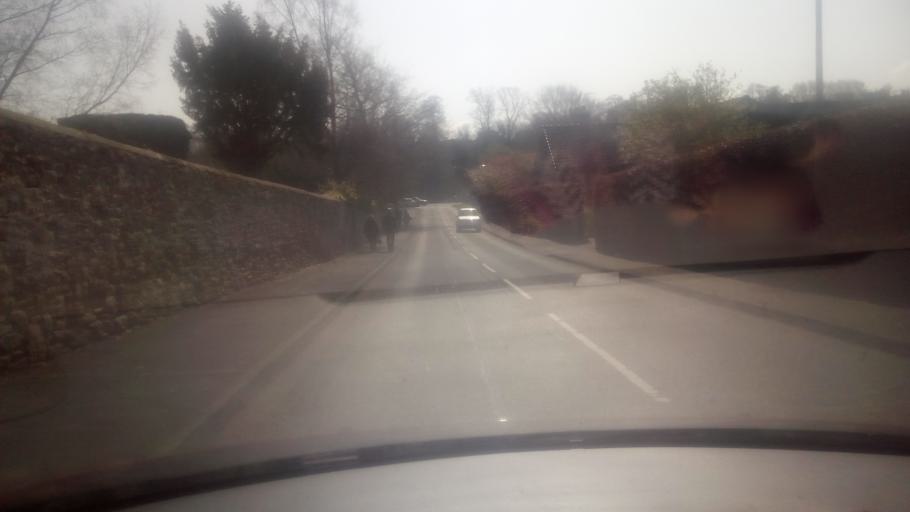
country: GB
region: Scotland
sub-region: The Scottish Borders
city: Kelso
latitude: 55.5969
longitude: -2.4302
